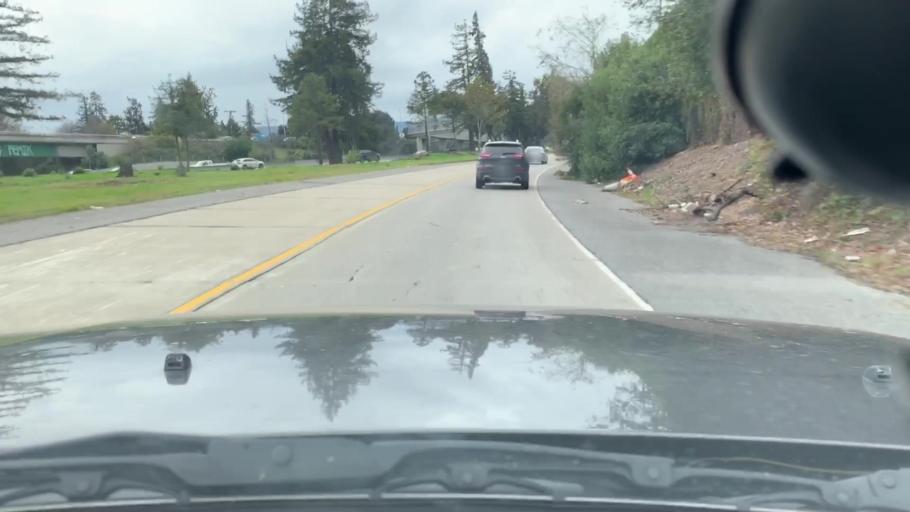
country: US
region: California
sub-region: Santa Clara County
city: Burbank
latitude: 37.3180
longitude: -121.9420
